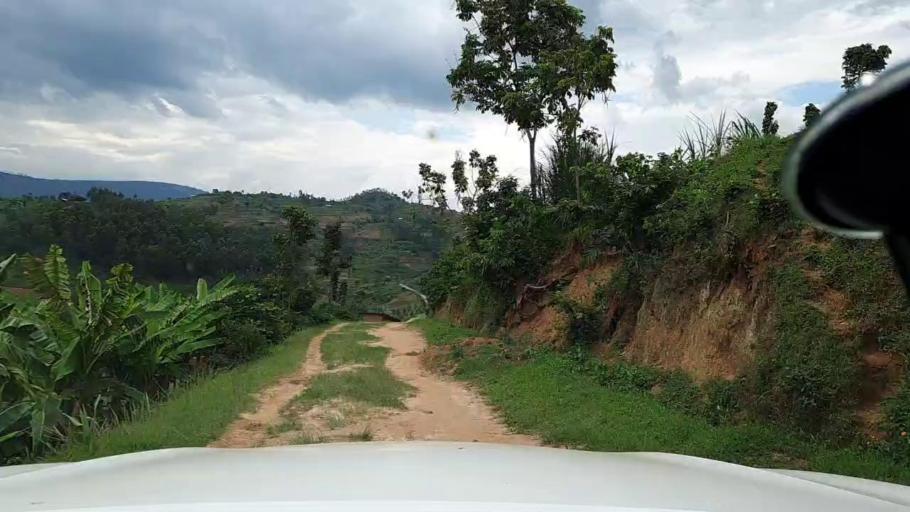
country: RW
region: Southern Province
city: Gitarama
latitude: -1.8167
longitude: 29.8010
